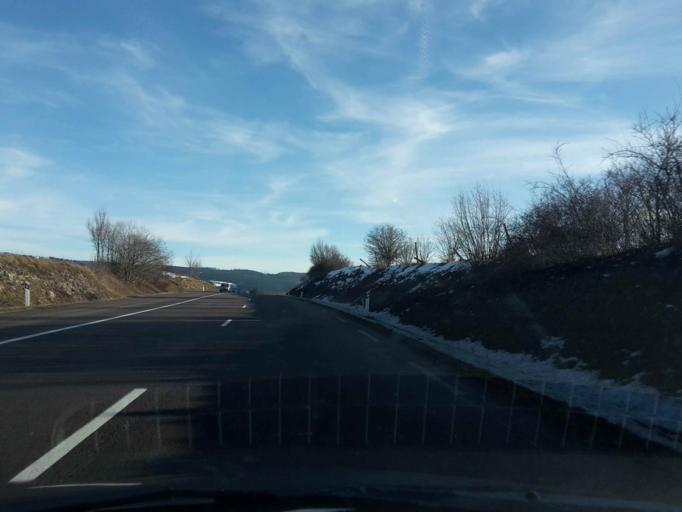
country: FR
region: Franche-Comte
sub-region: Departement du Doubs
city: Valdahon
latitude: 47.1064
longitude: 6.3210
